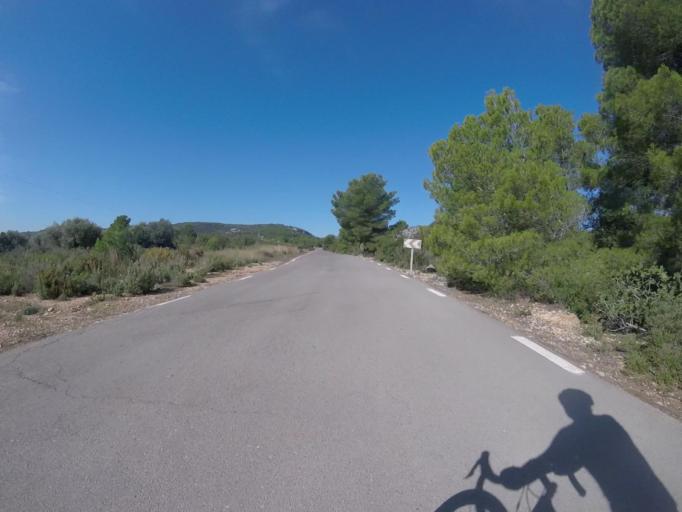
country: ES
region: Valencia
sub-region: Provincia de Castello
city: Sarratella
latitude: 40.2714
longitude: 0.0574
